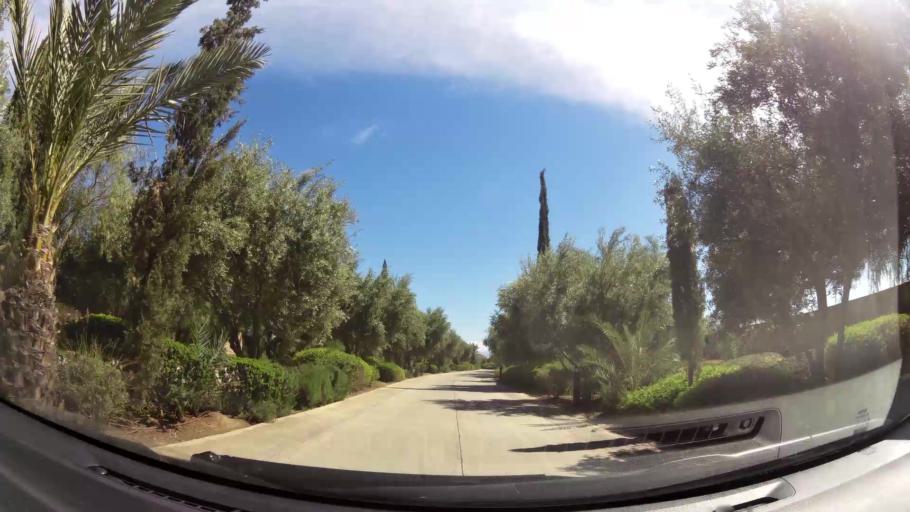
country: MA
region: Marrakech-Tensift-Al Haouz
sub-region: Marrakech
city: Marrakesh
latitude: 31.6033
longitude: -7.9534
